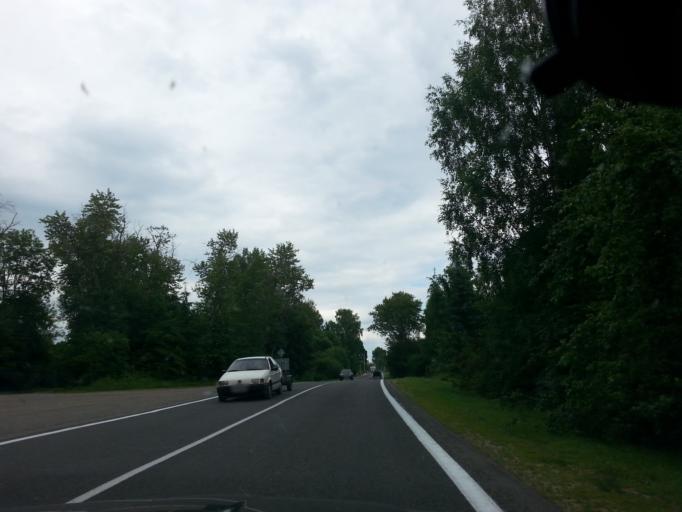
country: BY
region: Minsk
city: Narach
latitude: 54.8970
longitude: 26.7588
